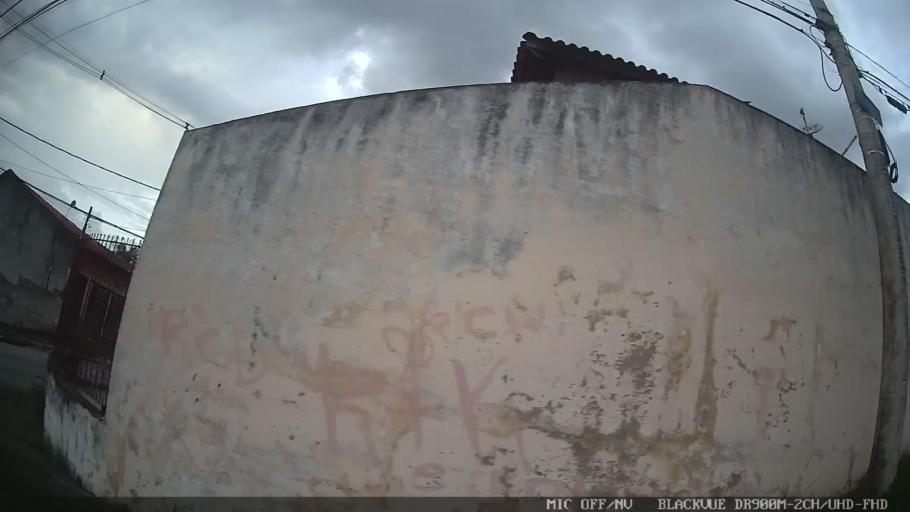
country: BR
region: Sao Paulo
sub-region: Mogi das Cruzes
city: Mogi das Cruzes
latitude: -23.5455
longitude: -46.1922
